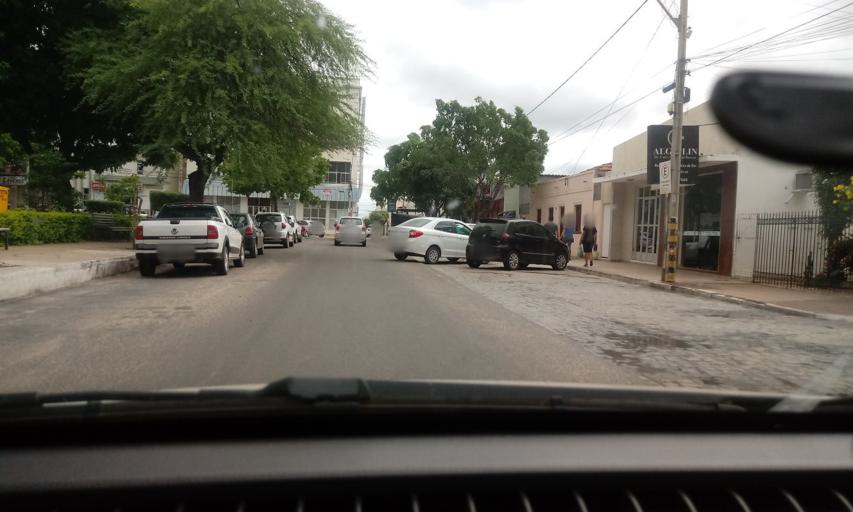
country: BR
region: Bahia
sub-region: Guanambi
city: Guanambi
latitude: -14.2229
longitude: -42.7790
